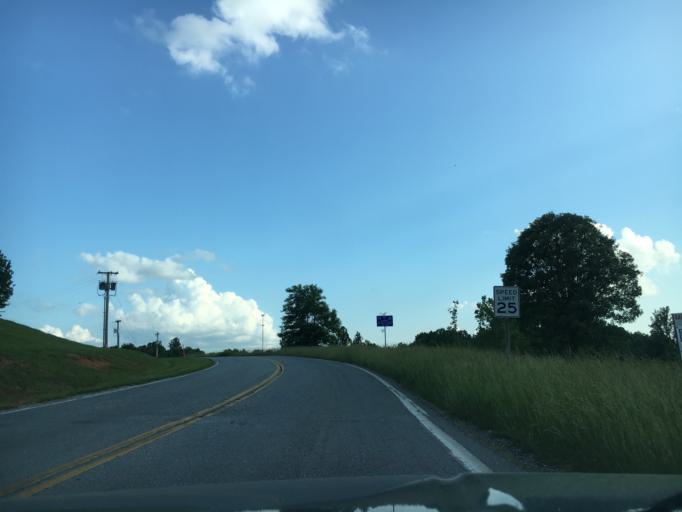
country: US
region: Virginia
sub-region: Bedford County
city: Forest
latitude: 37.3791
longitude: -79.2528
